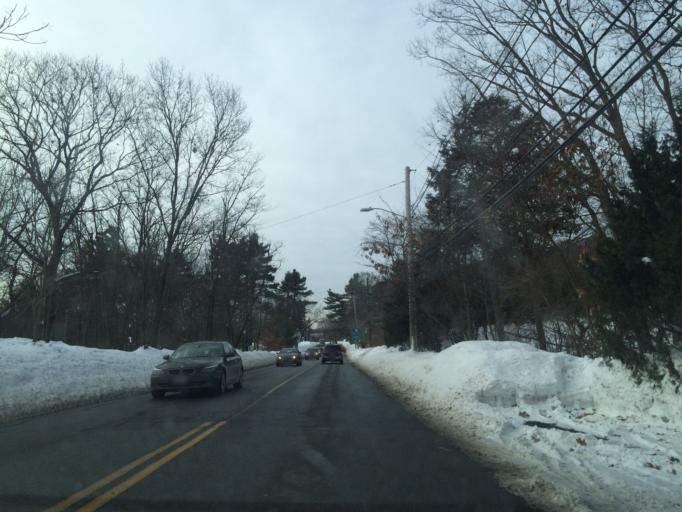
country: US
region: Massachusetts
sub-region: Middlesex County
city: Waltham
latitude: 42.3468
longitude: -71.2633
